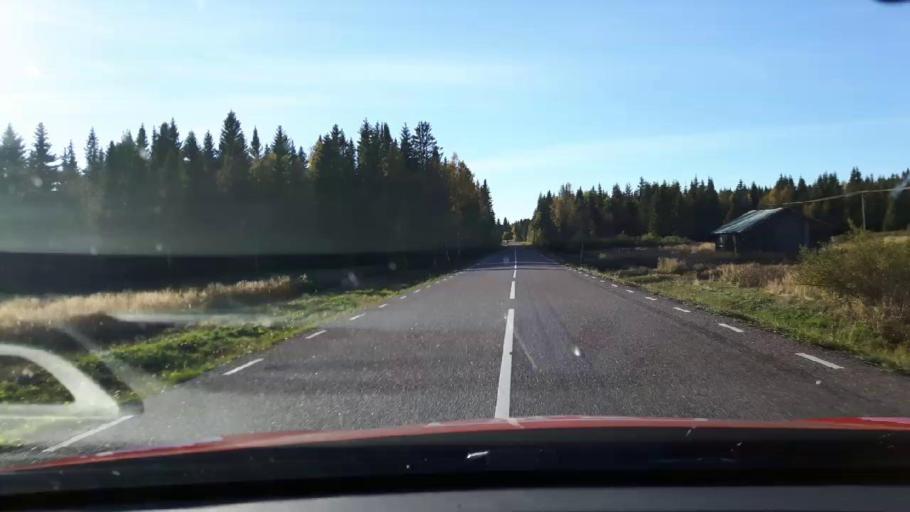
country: SE
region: Jaemtland
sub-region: Stroemsunds Kommun
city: Stroemsund
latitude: 63.8644
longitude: 15.1487
